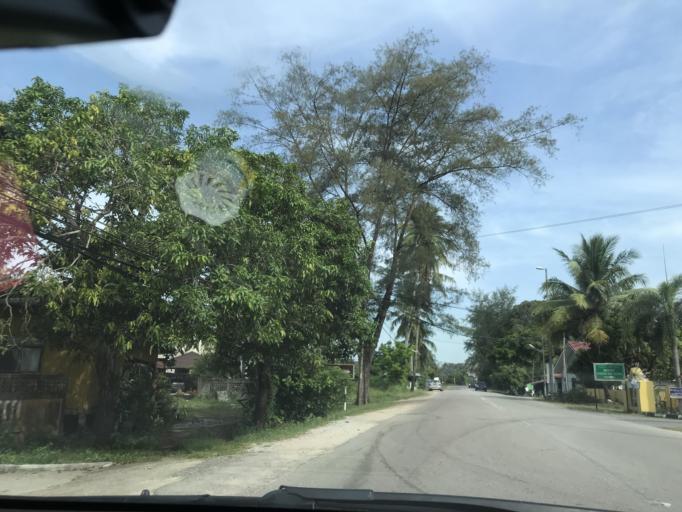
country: MY
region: Kelantan
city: Tumpat
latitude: 6.2147
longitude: 102.1270
